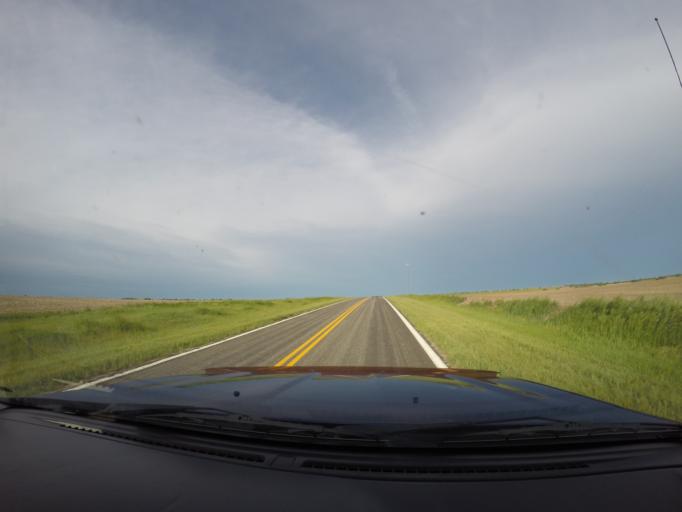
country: US
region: Kansas
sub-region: Smith County
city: Smith Center
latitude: 39.8282
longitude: -98.5696
